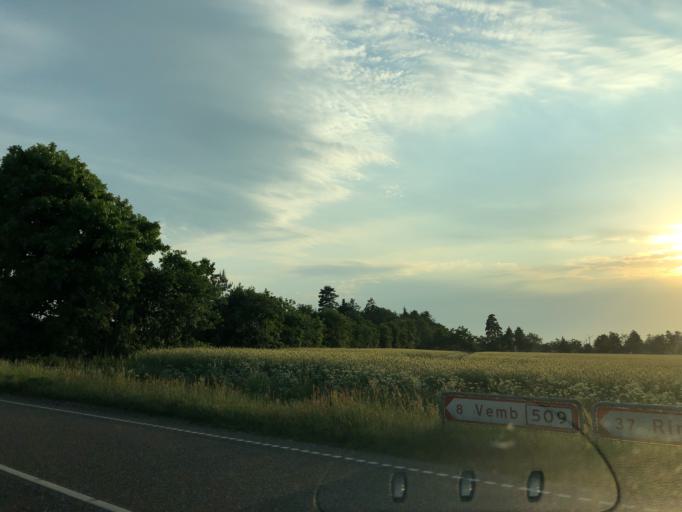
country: DK
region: Central Jutland
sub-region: Holstebro Kommune
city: Ulfborg
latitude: 56.3743
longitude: 8.4433
